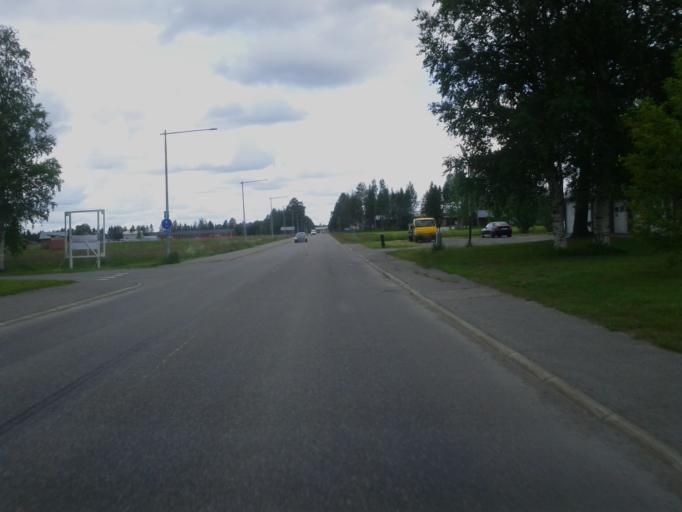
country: SE
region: Vaesterbotten
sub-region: Mala Kommun
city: Mala
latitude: 65.1874
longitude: 18.7341
